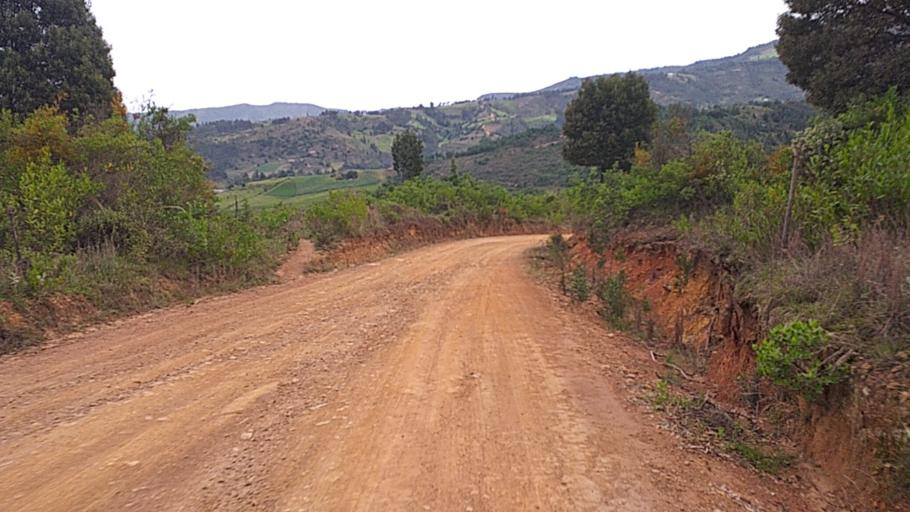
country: CO
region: Boyaca
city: Floresta
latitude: 5.8797
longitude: -72.9118
